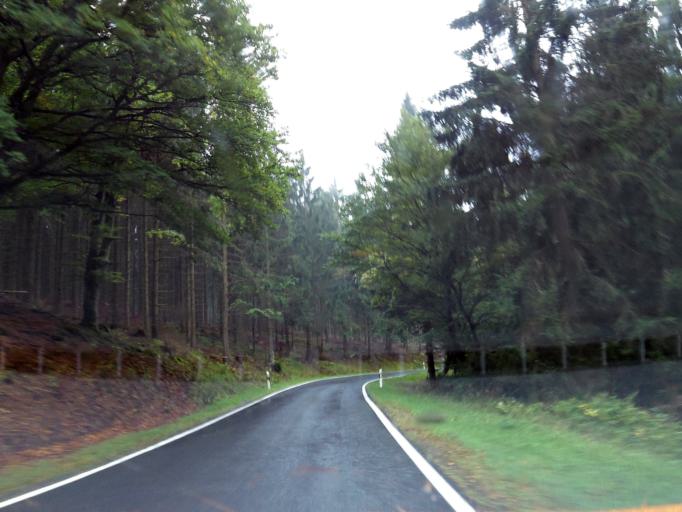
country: DE
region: Saxony-Anhalt
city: Hasselfelde
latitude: 51.6495
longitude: 10.8345
